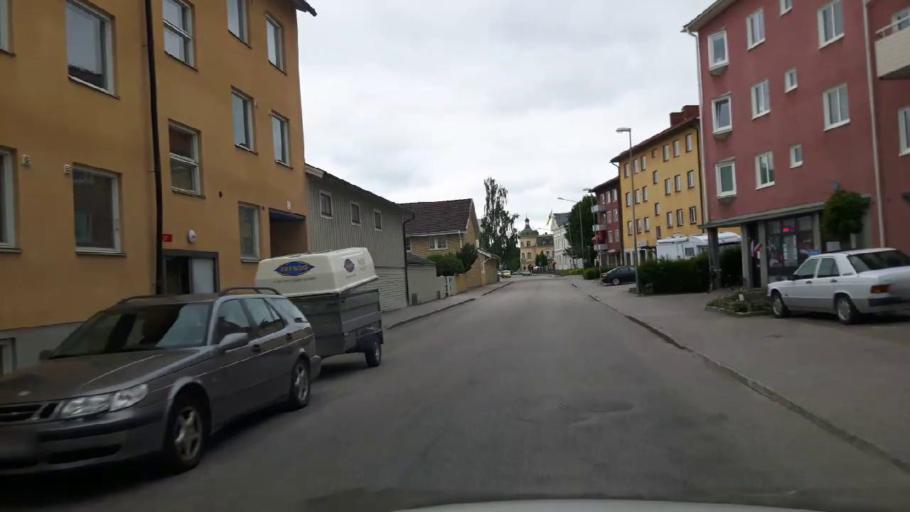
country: SE
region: Vaestmanland
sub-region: Kopings Kommun
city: Koping
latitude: 59.5155
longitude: 15.9906
